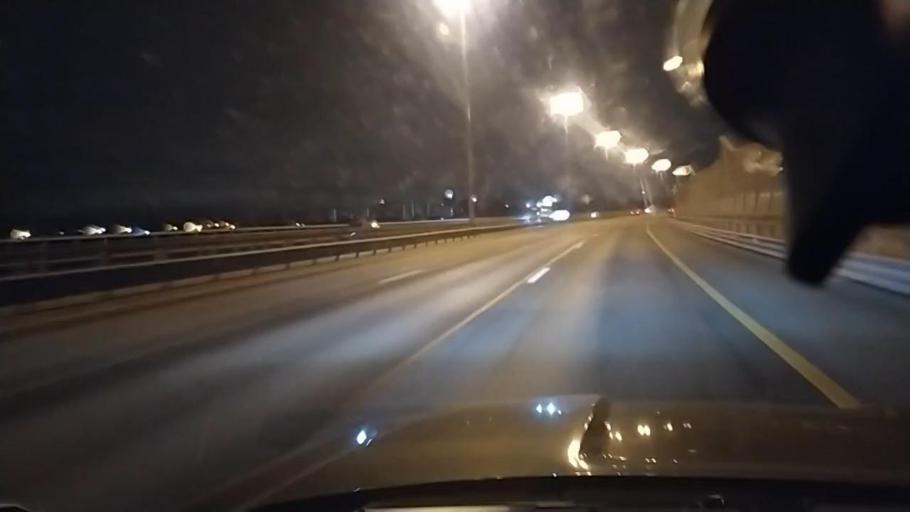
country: RU
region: Leningrad
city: Untolovo
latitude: 60.0382
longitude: 30.1735
